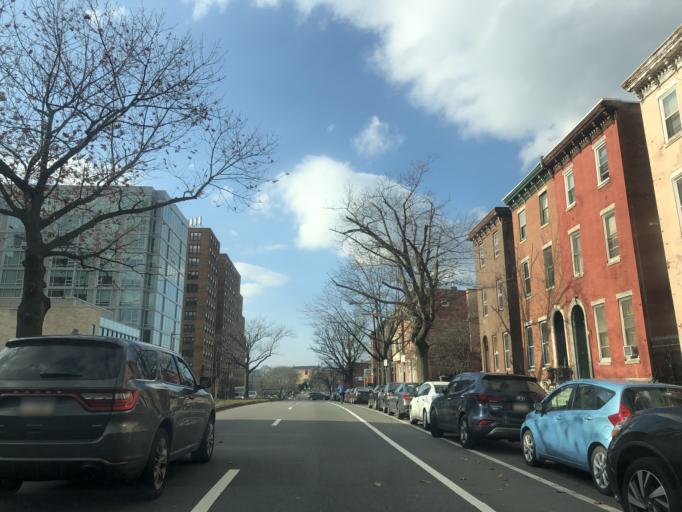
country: US
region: Pennsylvania
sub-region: Philadelphia County
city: Philadelphia
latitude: 39.9640
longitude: -75.1729
